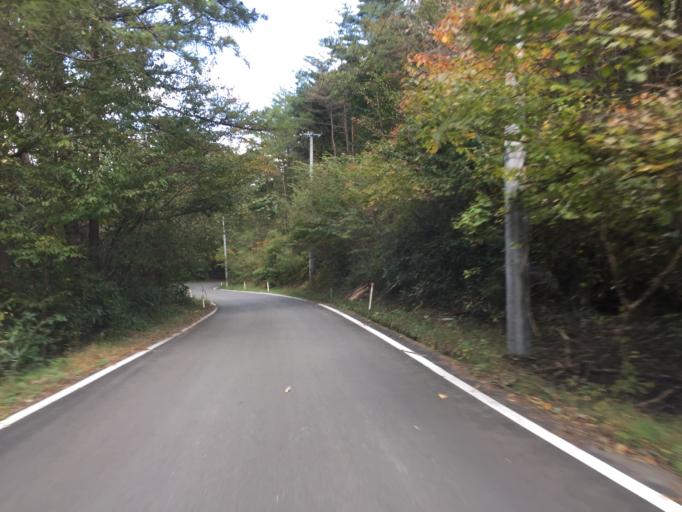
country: JP
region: Miyagi
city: Marumori
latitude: 37.8239
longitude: 140.8068
